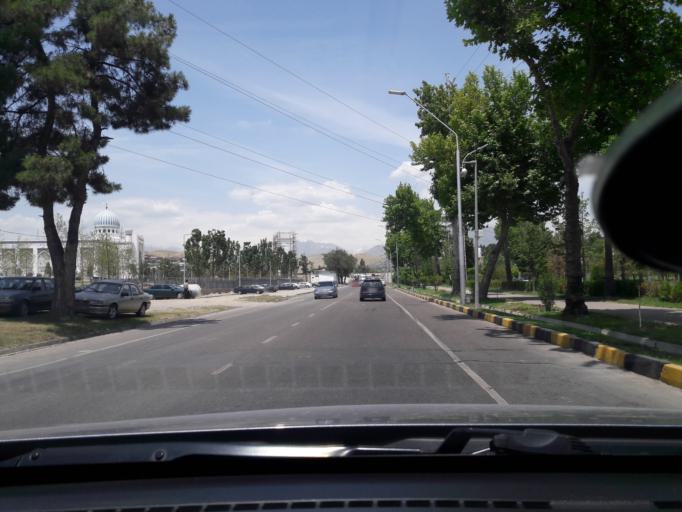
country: TJ
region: Dushanbe
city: Dushanbe
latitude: 38.5946
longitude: 68.7663
